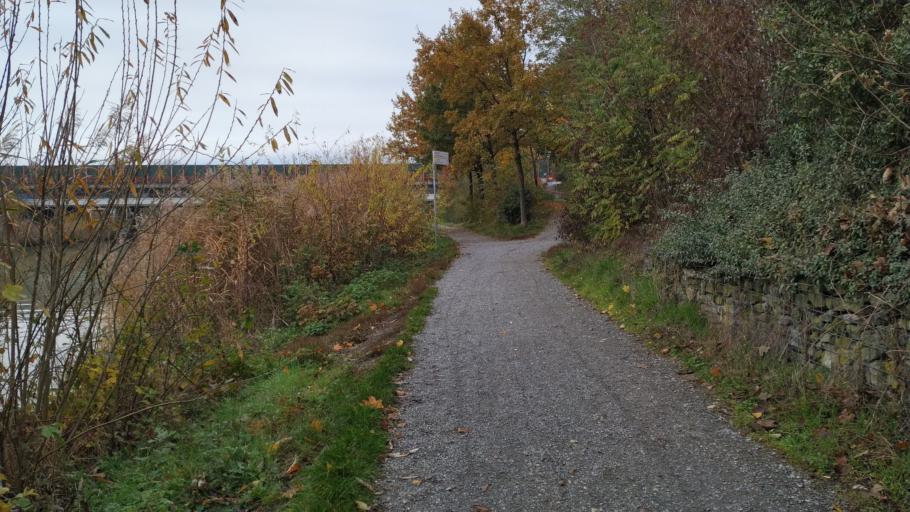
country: DE
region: Lower Saxony
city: Isernhagen Farster Bauerschaft
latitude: 52.4027
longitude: 9.8179
